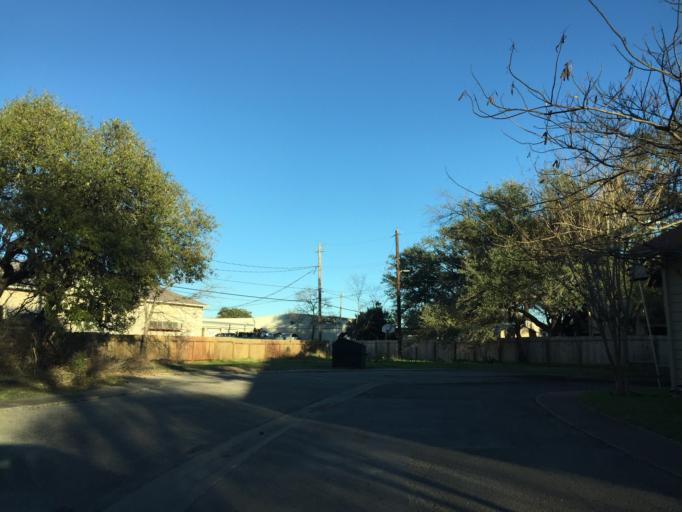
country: US
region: Texas
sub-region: Williamson County
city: Jollyville
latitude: 30.4374
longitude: -97.7784
